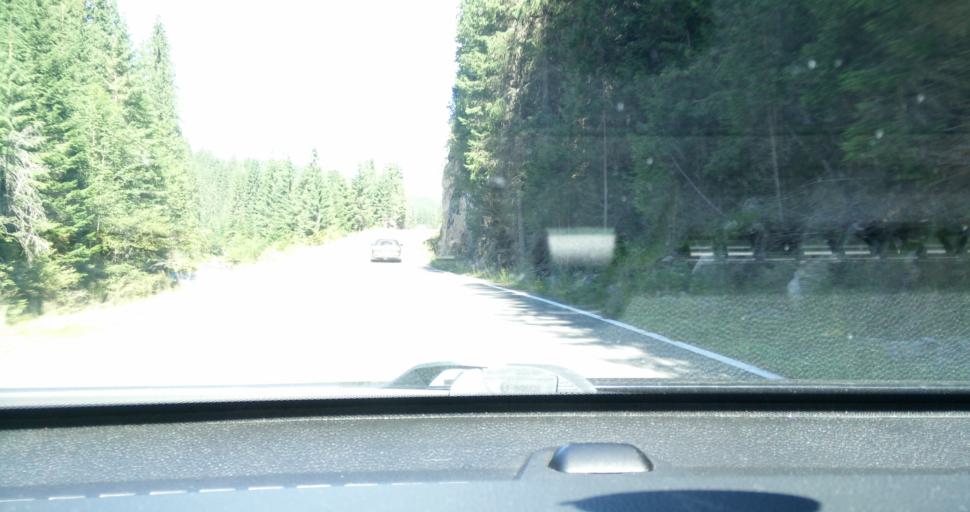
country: RO
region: Alba
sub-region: Comuna Sugag
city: Sugag
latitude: 45.5275
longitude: 23.6476
